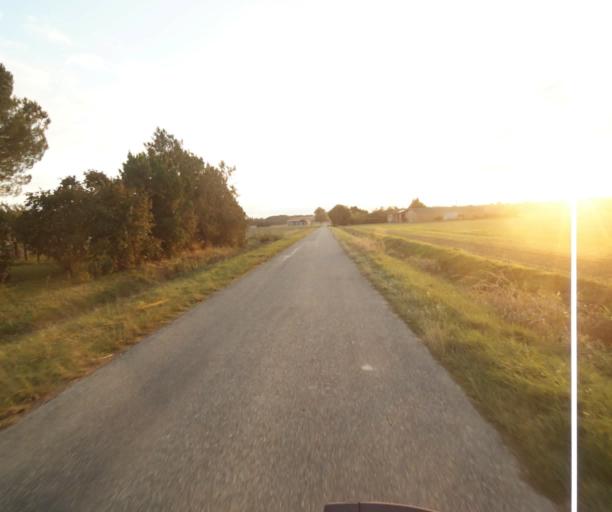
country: FR
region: Midi-Pyrenees
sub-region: Departement du Tarn-et-Garonne
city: Verdun-sur-Garonne
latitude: 43.8346
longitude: 1.2198
